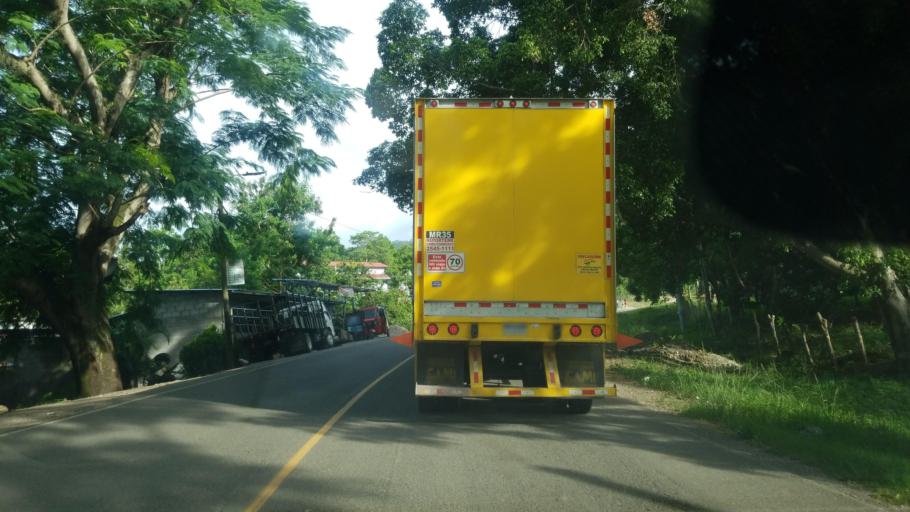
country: HN
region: Santa Barbara
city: Ilama
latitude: 15.0654
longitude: -88.2258
